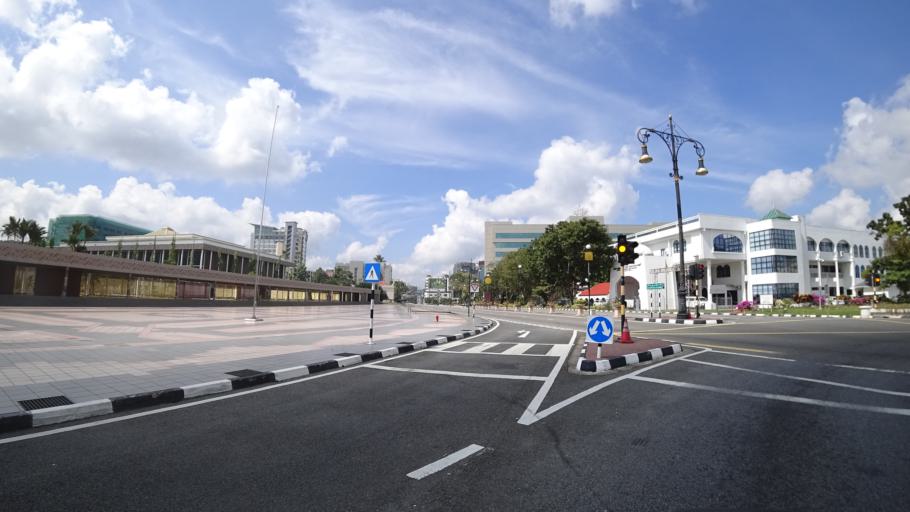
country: BN
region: Brunei and Muara
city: Bandar Seri Begawan
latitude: 4.8924
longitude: 114.9421
